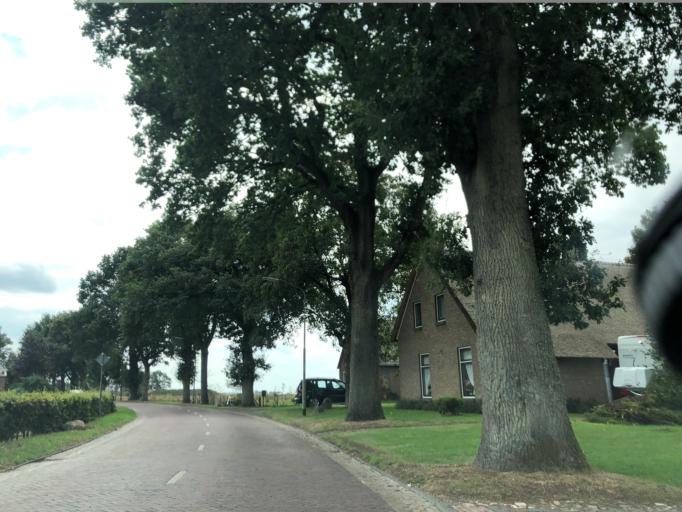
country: NL
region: Drenthe
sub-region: Gemeente Borger-Odoorn
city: Borger
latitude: 52.9047
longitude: 6.8110
